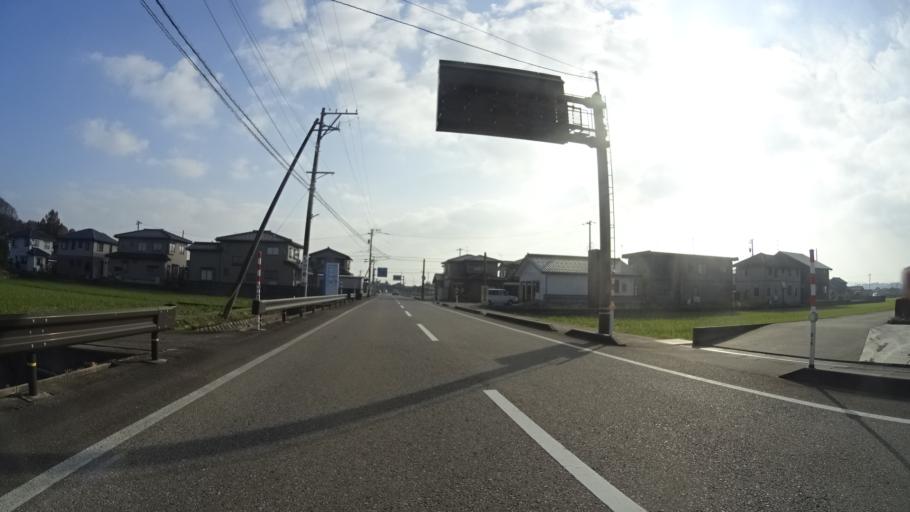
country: JP
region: Toyama
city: Himi
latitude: 36.8766
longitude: 136.9725
